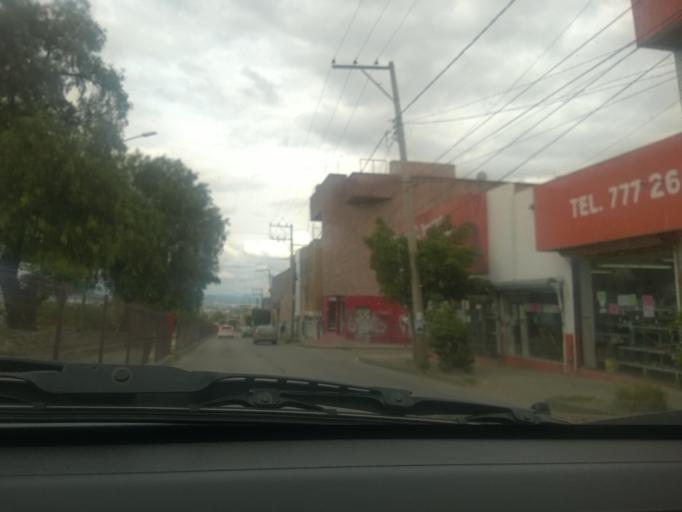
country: MX
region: Guanajuato
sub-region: Leon
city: La Ermita
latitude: 21.1328
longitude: -101.7138
